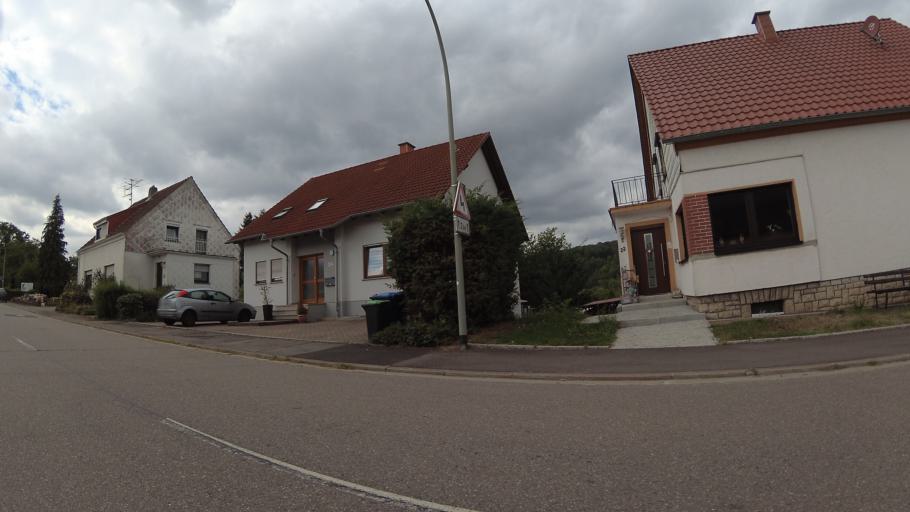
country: FR
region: Lorraine
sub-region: Departement de la Moselle
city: Sarreinsming
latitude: 49.1449
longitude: 7.1107
